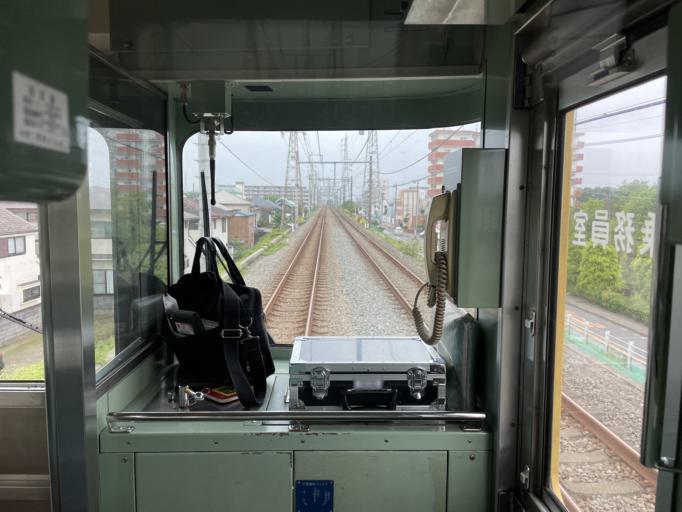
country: JP
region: Tokyo
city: Hino
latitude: 35.7286
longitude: 139.3900
